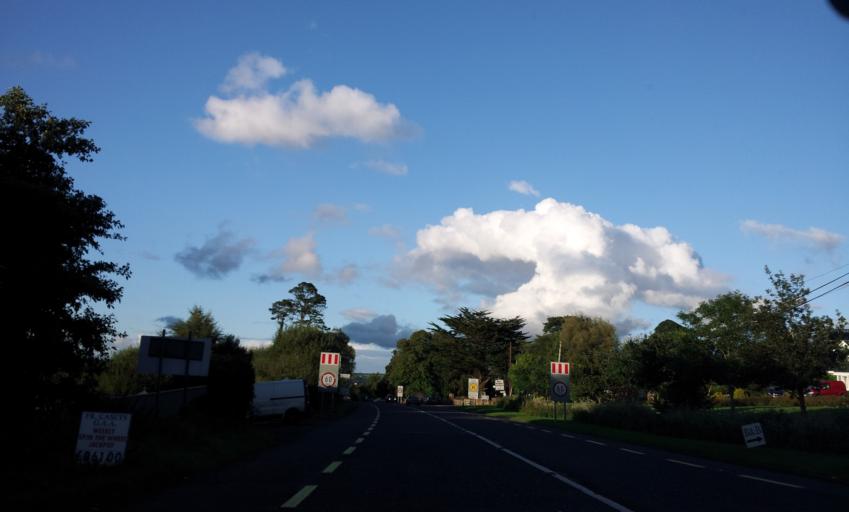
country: IE
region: Munster
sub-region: County Limerick
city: Abbeyfeale
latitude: 52.3716
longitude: -9.3143
